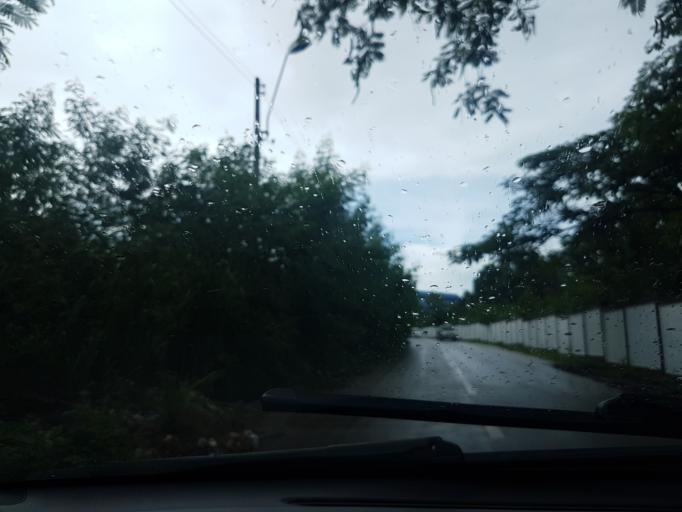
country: TH
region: Lampang
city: Lampang
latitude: 18.3001
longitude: 99.4747
